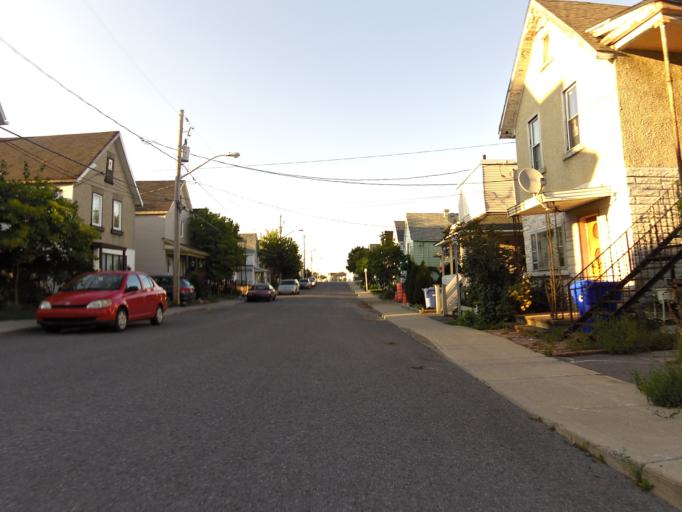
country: CA
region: Ontario
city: Ottawa
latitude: 45.4340
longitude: -75.7142
